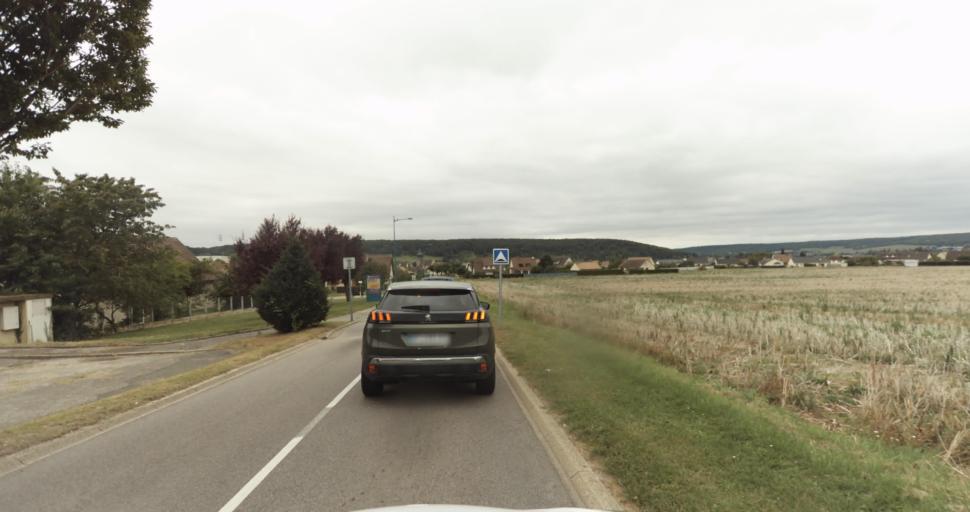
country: FR
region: Haute-Normandie
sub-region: Departement de l'Eure
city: Gravigny
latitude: 49.0450
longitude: 1.1703
